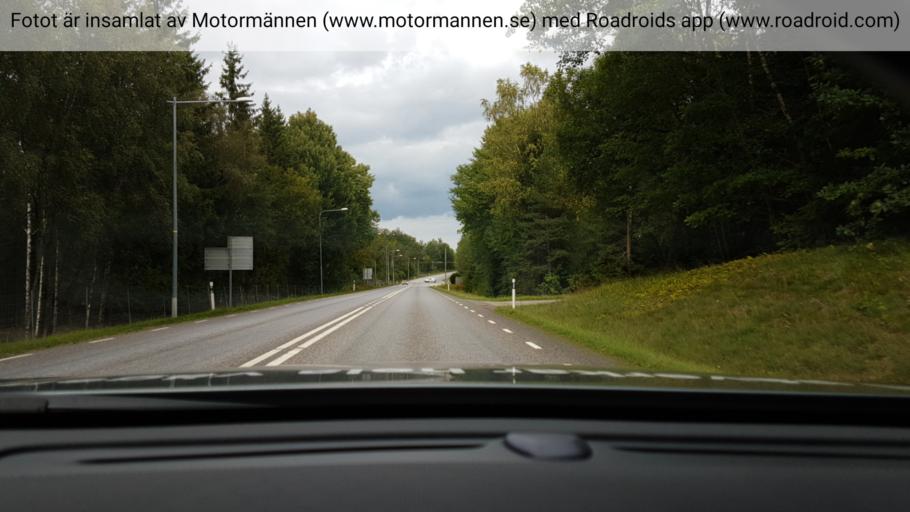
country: SE
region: Halland
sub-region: Hylte Kommun
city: Hyltebruk
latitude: 56.9894
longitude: 13.2180
